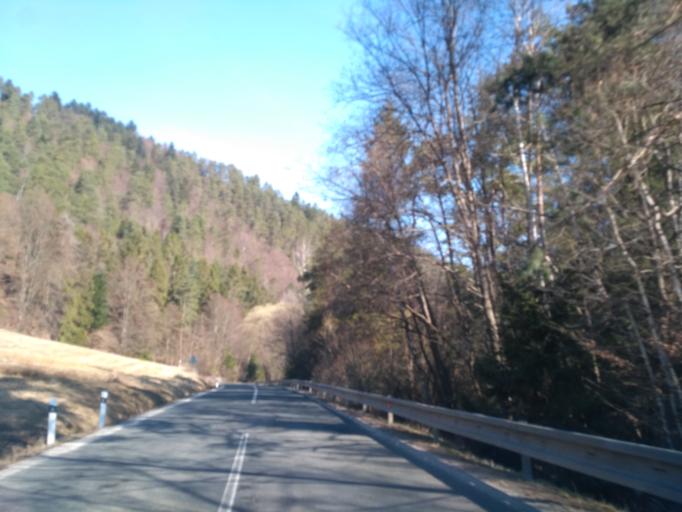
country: SK
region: Kosicky
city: Medzev
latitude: 48.7784
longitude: 20.7897
